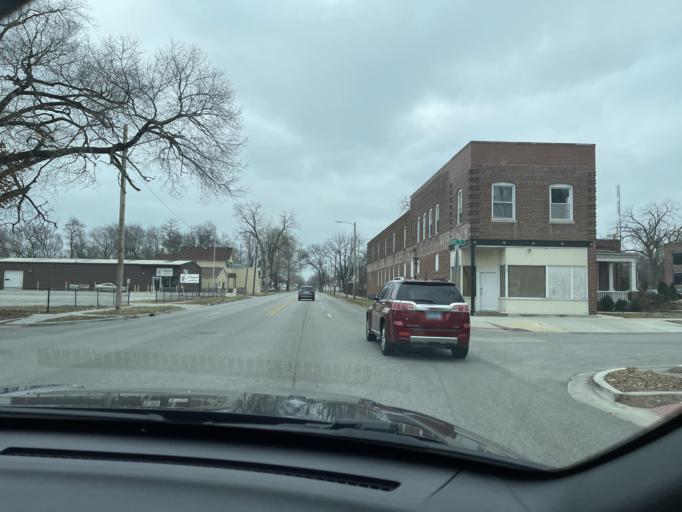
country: US
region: Illinois
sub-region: Sangamon County
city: Springfield
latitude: 39.7947
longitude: -89.6398
